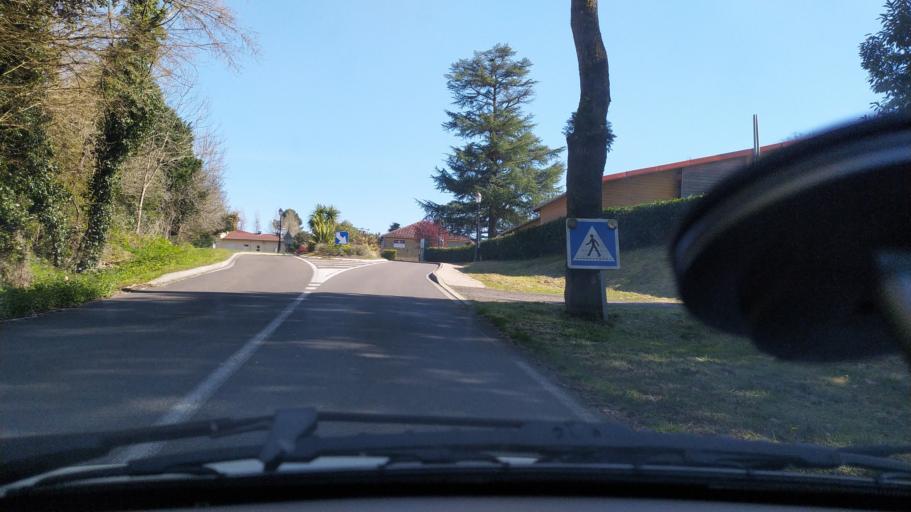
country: FR
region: Midi-Pyrenees
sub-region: Departement du Gers
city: Le Houga
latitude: 43.7701
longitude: -0.1253
